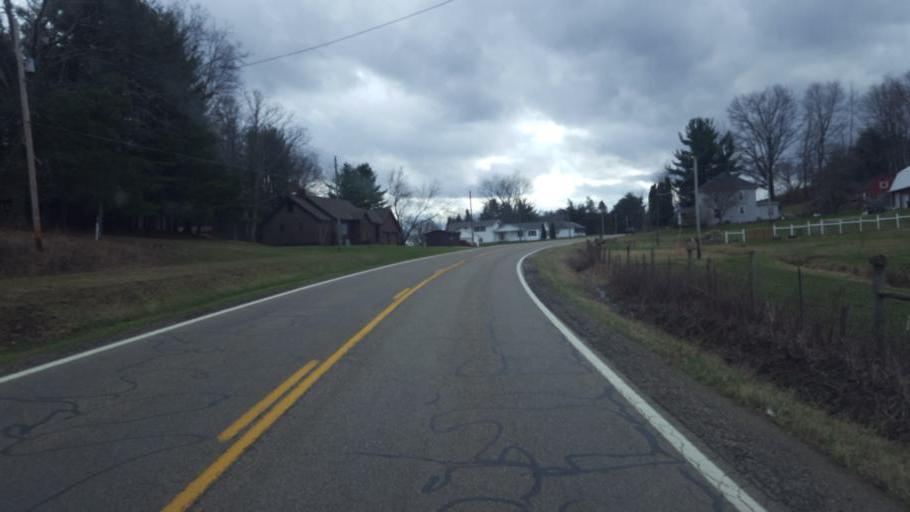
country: US
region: Ohio
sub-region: Muskingum County
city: Frazeysburg
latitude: 40.0947
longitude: -82.1674
